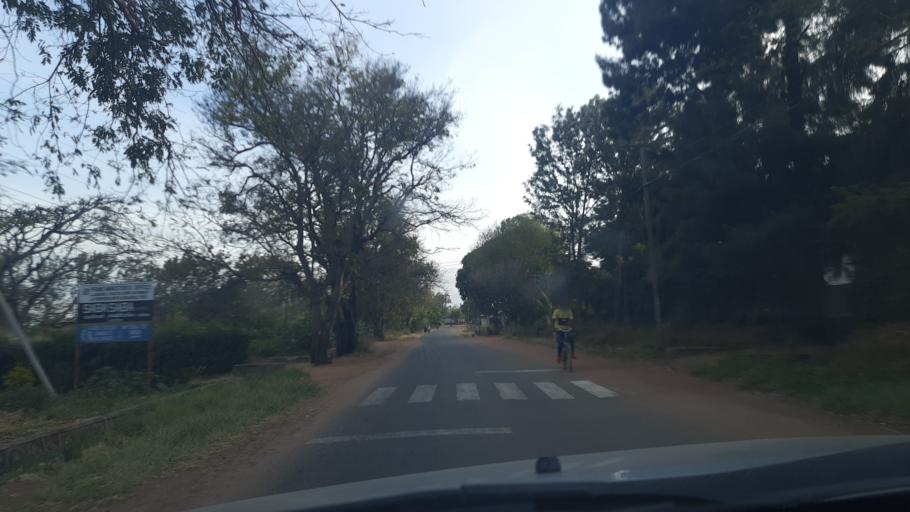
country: TZ
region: Singida
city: Singida
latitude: -4.8126
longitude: 34.7330
